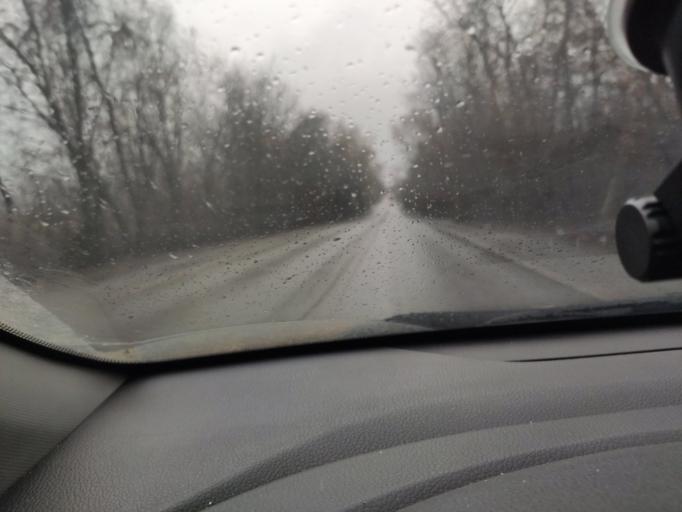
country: RU
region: Moskovskaya
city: Biryulevo Zapadnoye
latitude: 55.5690
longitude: 37.6485
